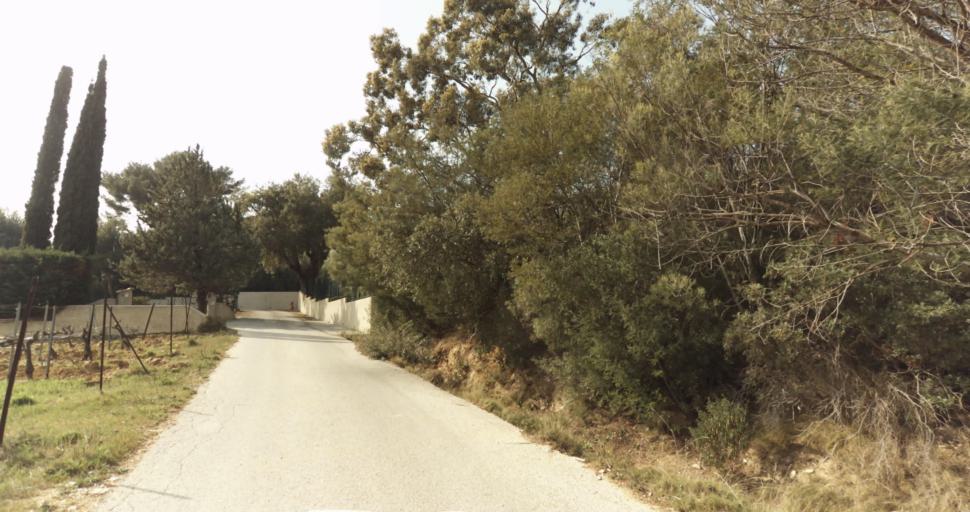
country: FR
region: Provence-Alpes-Cote d'Azur
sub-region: Departement du Var
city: Bormes-les-Mimosas
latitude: 43.1495
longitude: 6.3247
